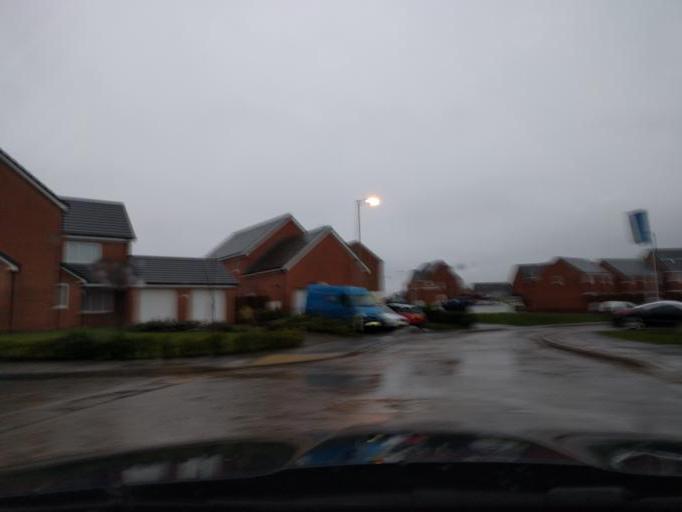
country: GB
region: England
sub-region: Northumberland
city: Newbiggin-by-the-Sea
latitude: 55.1800
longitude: -1.5437
